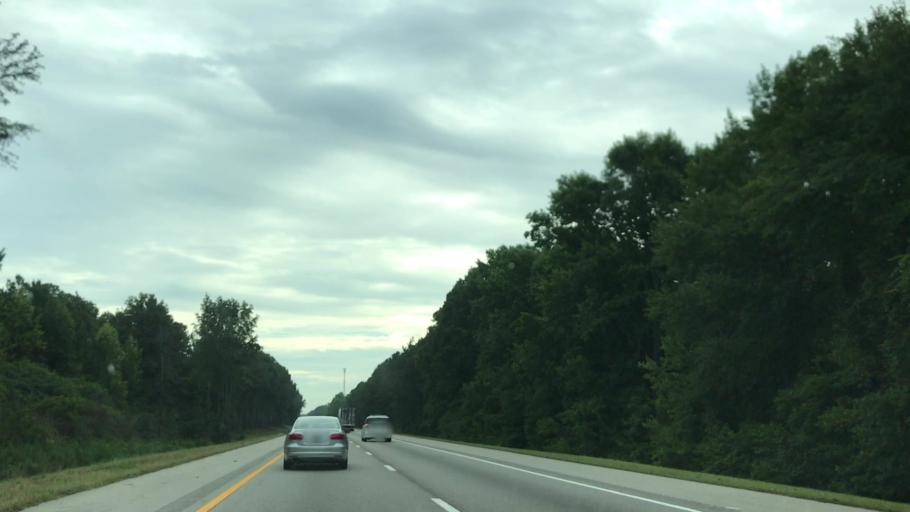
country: US
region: North Carolina
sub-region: Wilson County
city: Lucama
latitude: 35.6694
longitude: -78.0788
